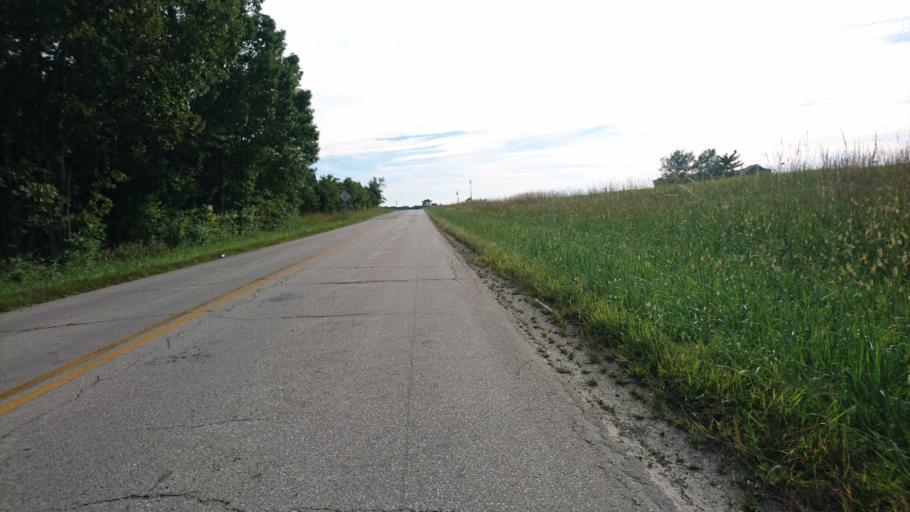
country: US
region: Missouri
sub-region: Crawford County
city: Cuba
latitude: 38.0947
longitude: -91.3641
